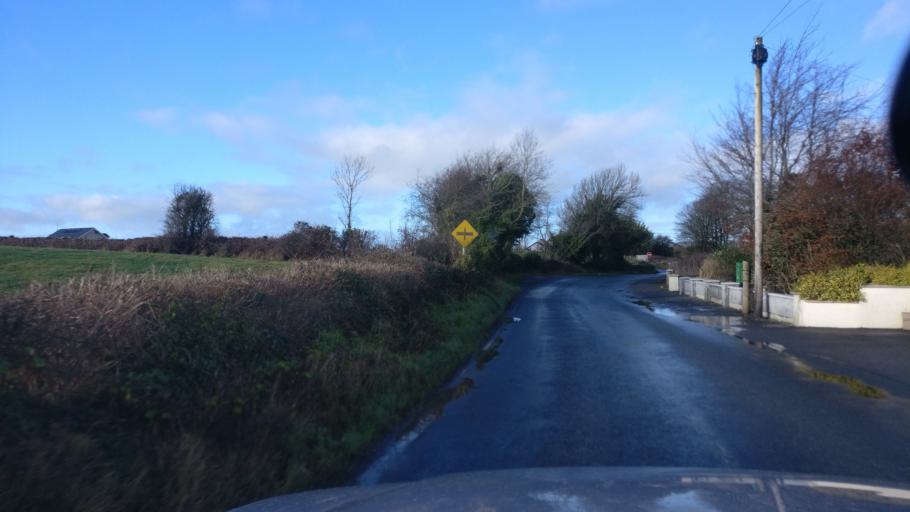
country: IE
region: Connaught
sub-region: County Galway
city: Athenry
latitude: 53.2709
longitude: -8.6937
